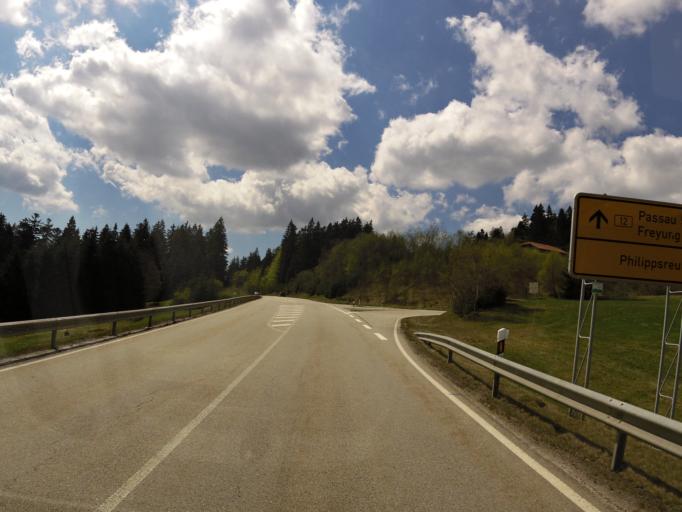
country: DE
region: Bavaria
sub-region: Lower Bavaria
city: Philippsreut
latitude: 48.8628
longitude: 13.6795
